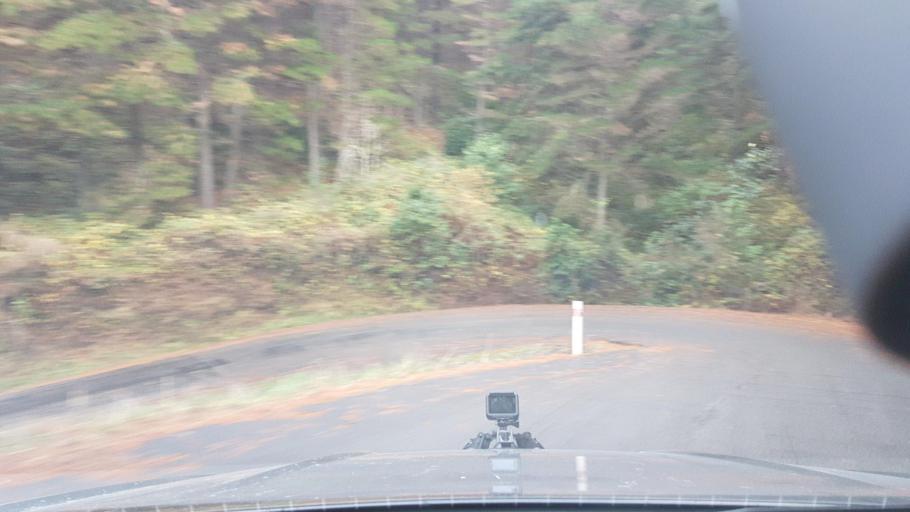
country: NZ
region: Nelson
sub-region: Nelson City
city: Nelson
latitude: -41.5821
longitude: 173.4166
